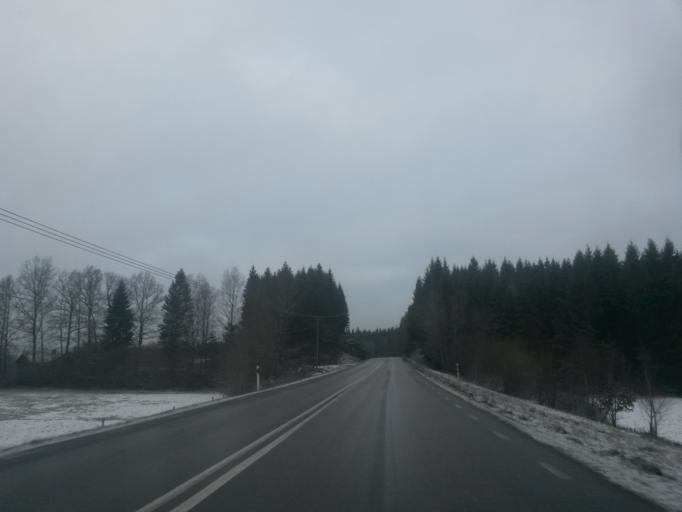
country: SE
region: Vaestra Goetaland
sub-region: Vargarda Kommun
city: Jonstorp
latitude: 58.0812
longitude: 12.6758
